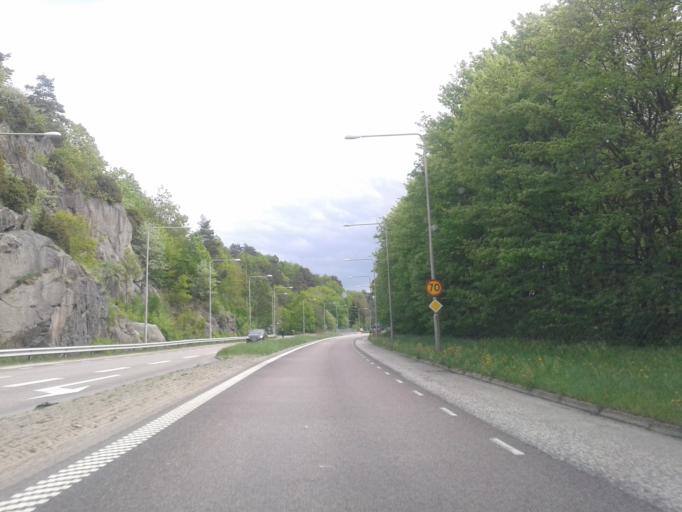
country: SE
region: Vaestra Goetaland
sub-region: Goteborg
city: Eriksbo
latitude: 57.7728
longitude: 12.0381
